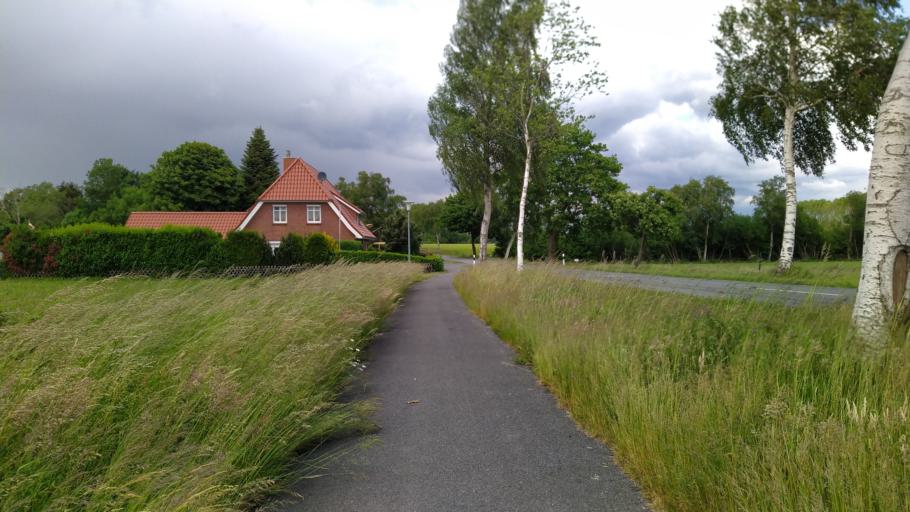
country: DE
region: Lower Saxony
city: Brest
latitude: 53.4553
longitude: 9.3837
